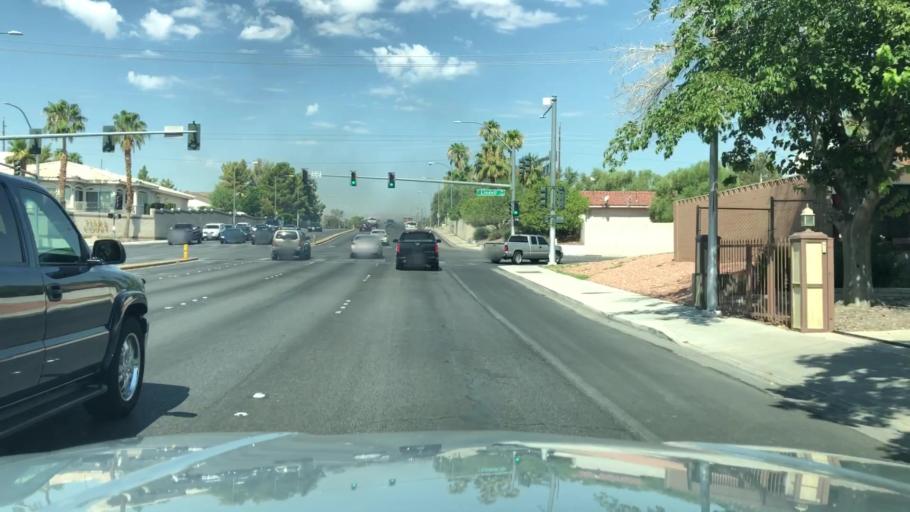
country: US
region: Nevada
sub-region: Clark County
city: Spring Valley
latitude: 36.1297
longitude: -115.2159
